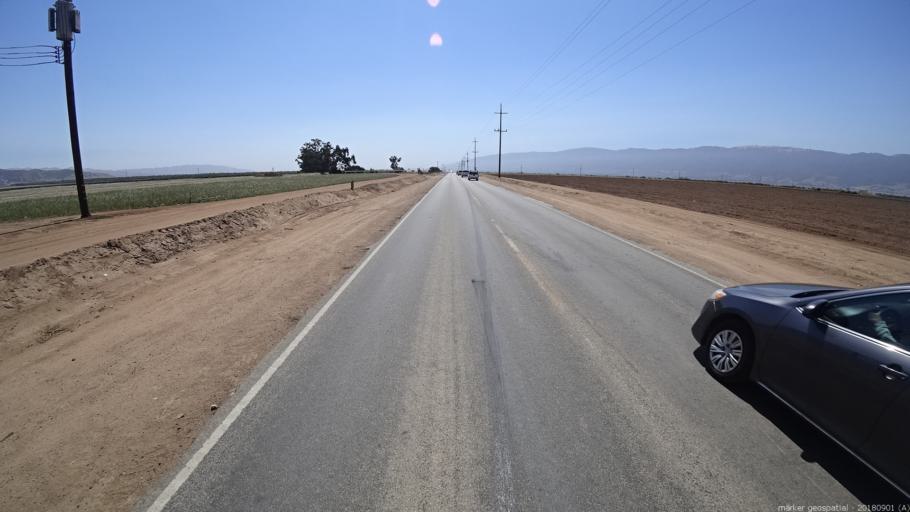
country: US
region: California
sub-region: Monterey County
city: Chualar
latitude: 36.5855
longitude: -121.5000
